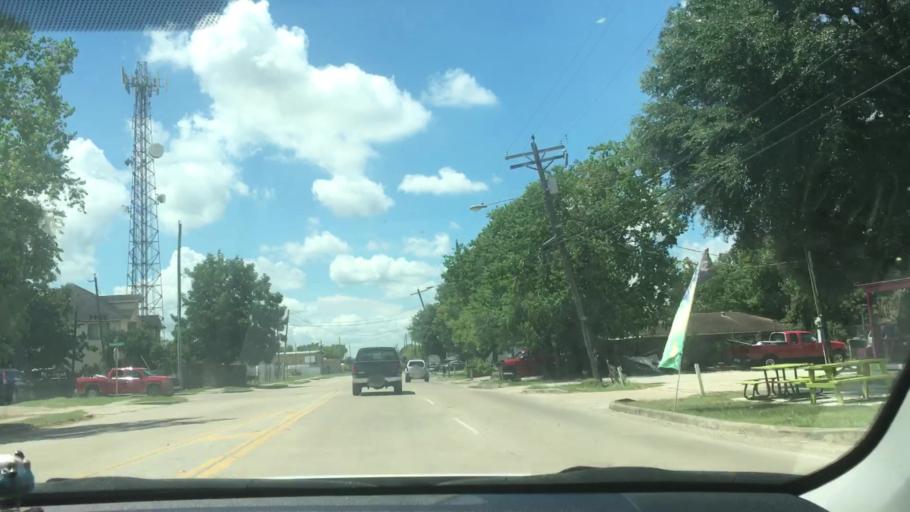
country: US
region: Texas
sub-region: Fort Bend County
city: Fifth Street
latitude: 29.5977
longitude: -95.5563
